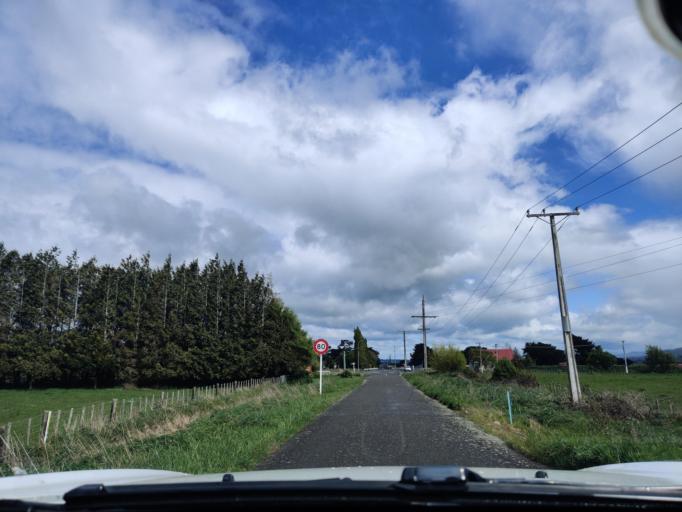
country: NZ
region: Manawatu-Wanganui
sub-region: Palmerston North City
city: Palmerston North
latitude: -40.3165
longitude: 175.8567
